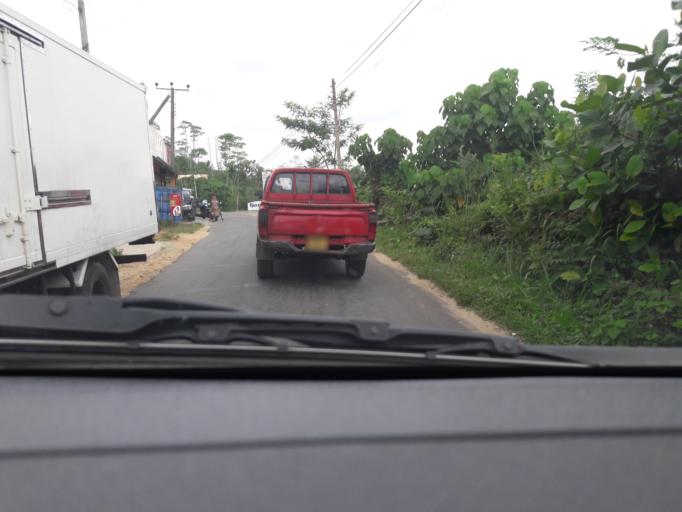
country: LK
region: Southern
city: Hikkaduwa
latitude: 6.2513
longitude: 80.2675
